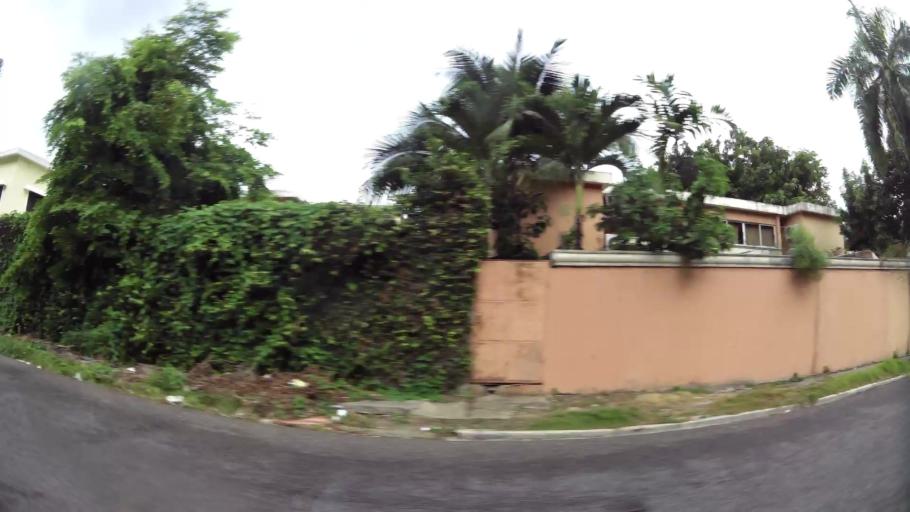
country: DO
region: Nacional
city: La Agustina
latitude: 18.5085
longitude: -69.9466
